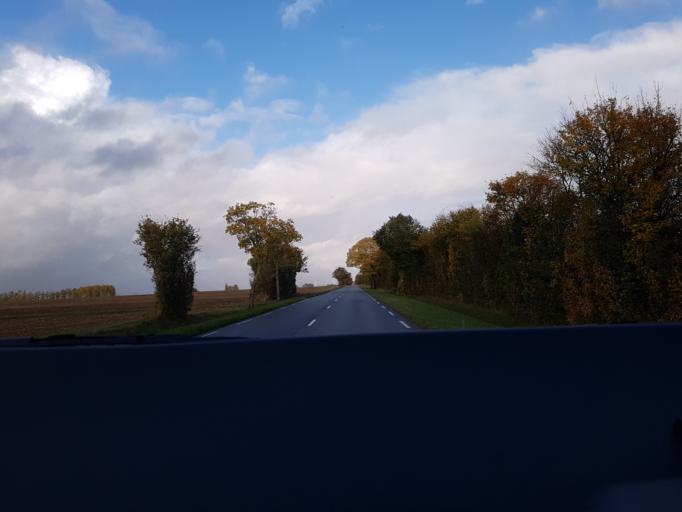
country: FR
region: Poitou-Charentes
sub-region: Departement des Deux-Sevres
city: Brioux-sur-Boutonne
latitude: 46.1148
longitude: -0.2479
